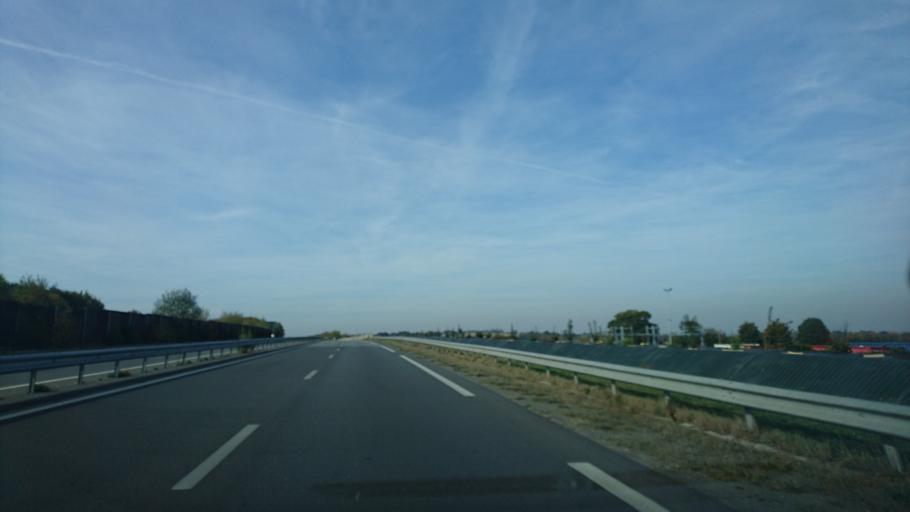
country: FR
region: Brittany
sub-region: Departement d'Ille-et-Vilaine
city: Corps-Nuds
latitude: 47.9744
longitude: -1.5443
